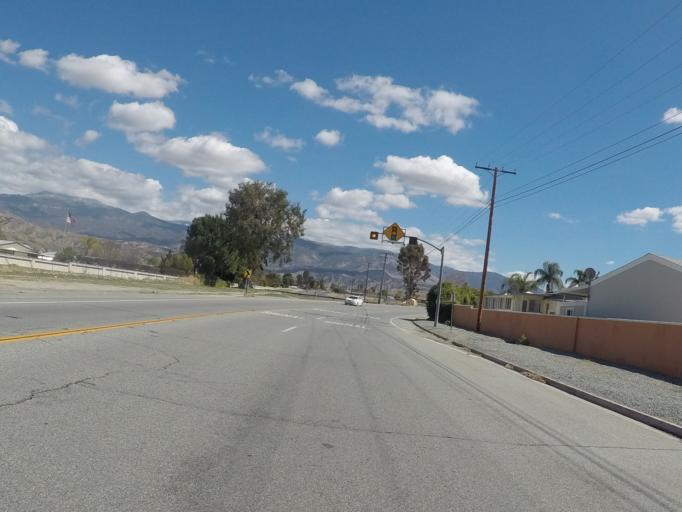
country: US
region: California
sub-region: Riverside County
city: Valle Vista
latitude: 33.7622
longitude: -116.9140
